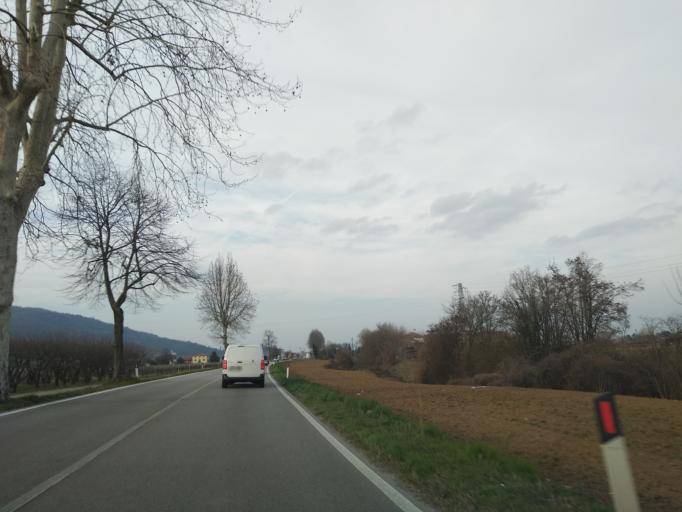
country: IT
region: Veneto
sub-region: Provincia di Vicenza
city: Ponte di Castegnero
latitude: 45.4503
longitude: 11.6013
